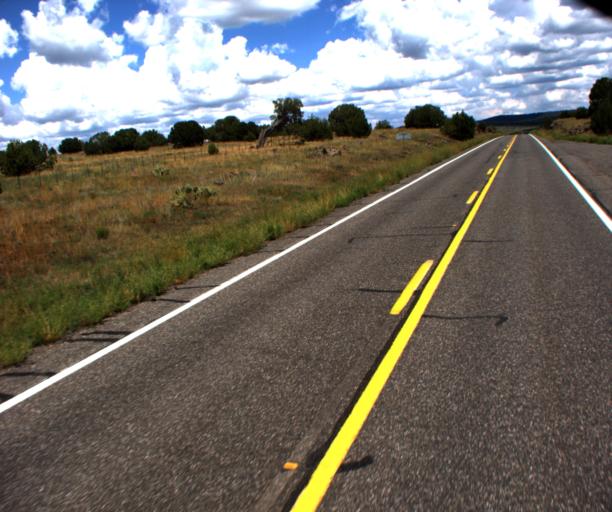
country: US
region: Arizona
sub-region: Gila County
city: Pine
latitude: 34.4909
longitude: -111.5949
